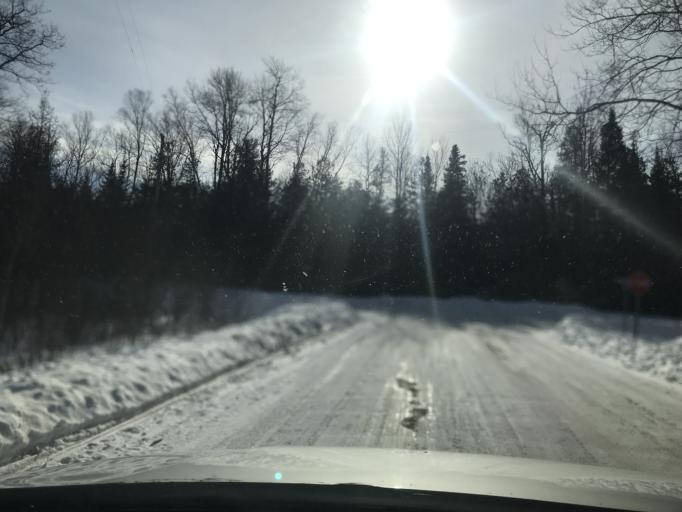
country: US
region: Wisconsin
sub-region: Oconto County
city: Gillett
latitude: 45.1487
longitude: -88.2247
